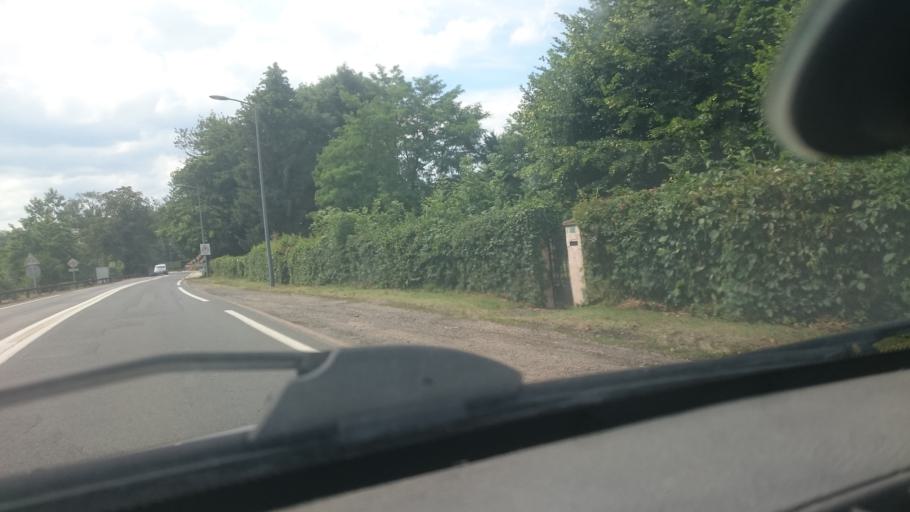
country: FR
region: Rhone-Alpes
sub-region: Departement du Rhone
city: Lozanne
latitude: 45.8587
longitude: 4.6887
